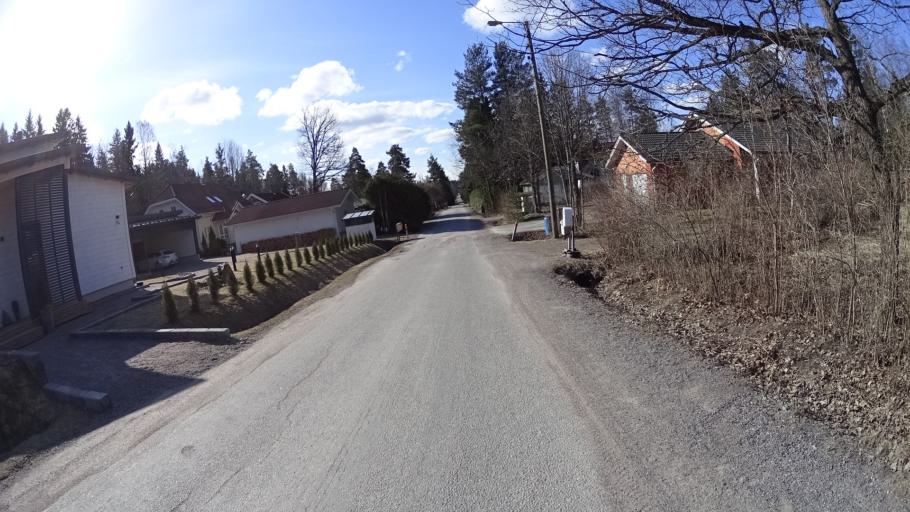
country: FI
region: Uusimaa
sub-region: Helsinki
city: Kilo
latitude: 60.2874
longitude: 24.7524
